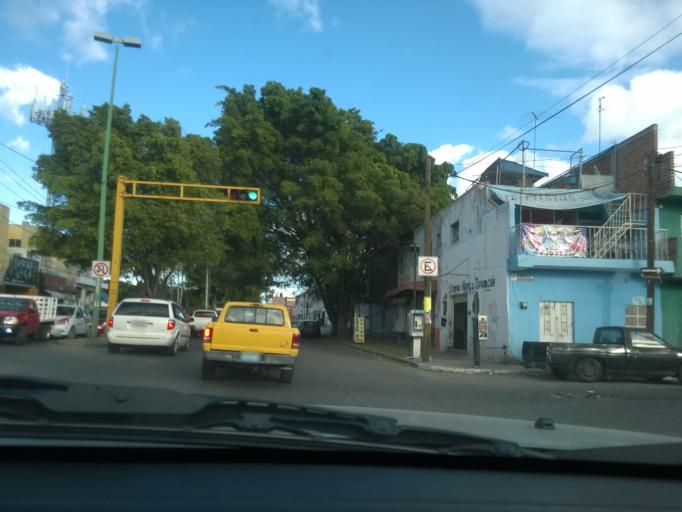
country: MX
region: Guanajuato
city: Leon
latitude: 21.1315
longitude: -101.6670
